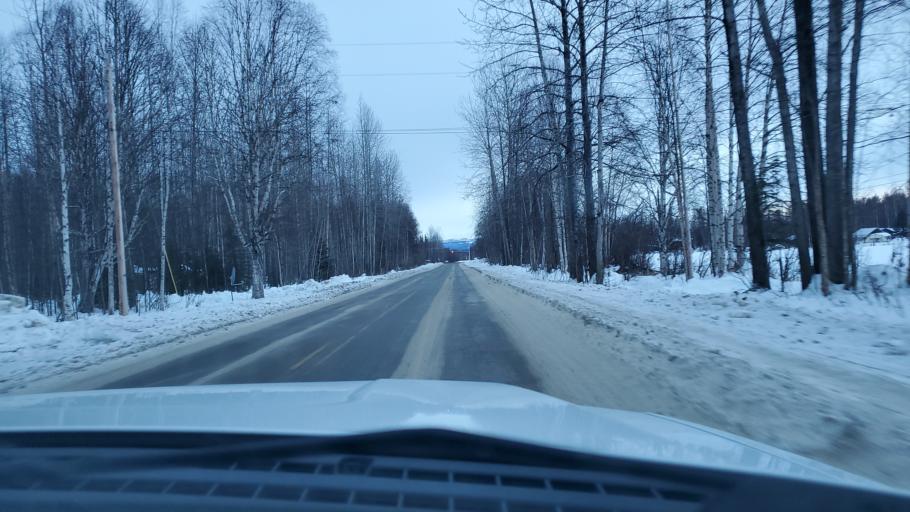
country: US
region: Alaska
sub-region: Matanuska-Susitna Borough
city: Y
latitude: 62.3163
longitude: -150.2415
